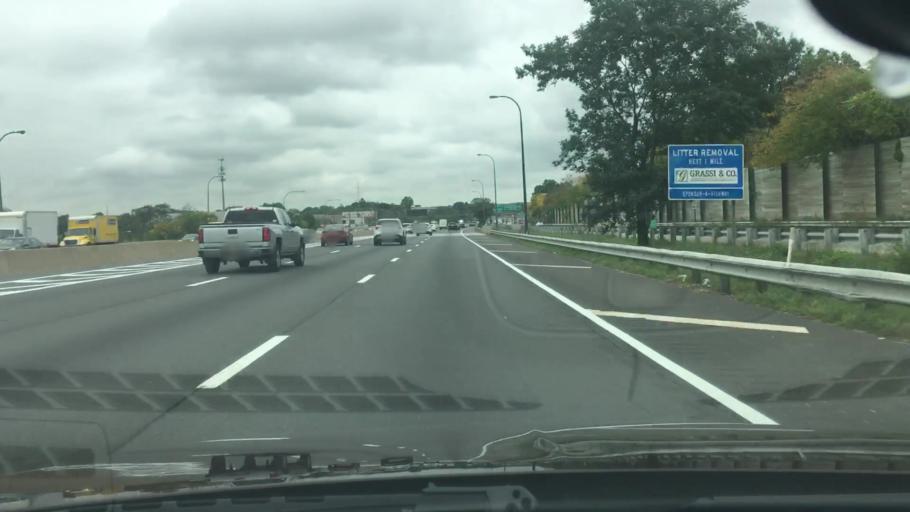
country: US
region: New York
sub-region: Nassau County
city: Jericho
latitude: 40.7943
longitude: -73.5124
